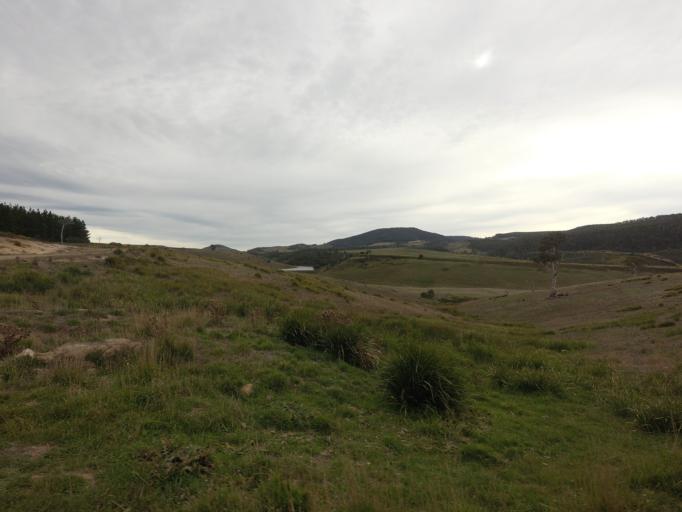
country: AU
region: Tasmania
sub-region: Derwent Valley
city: New Norfolk
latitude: -42.3972
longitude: 146.9130
